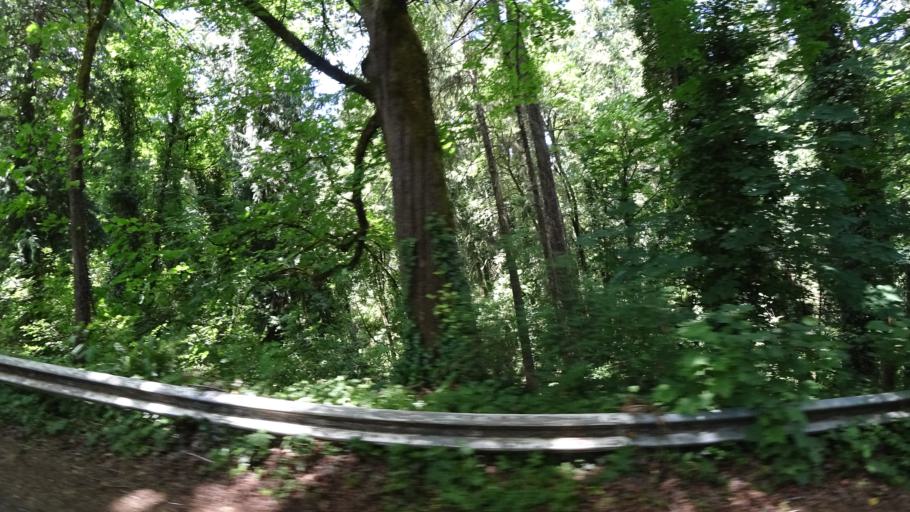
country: US
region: Oregon
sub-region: Washington County
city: West Haven
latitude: 45.5861
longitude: -122.7750
